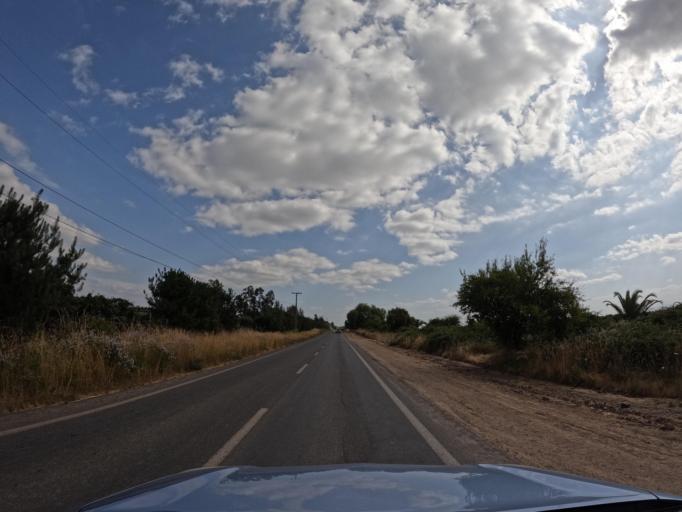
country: CL
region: Maule
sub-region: Provincia de Curico
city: Molina
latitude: -35.1850
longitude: -71.2952
